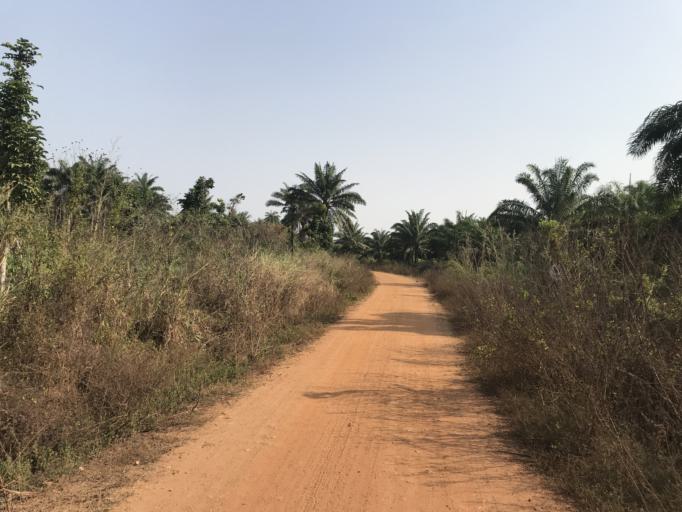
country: NG
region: Osun
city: Olupona
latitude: 7.6106
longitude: 4.1482
